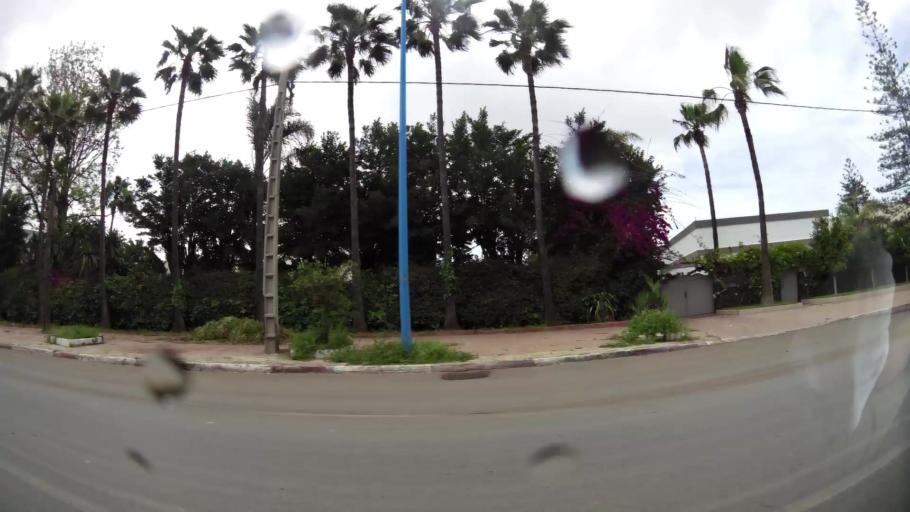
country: MA
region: Grand Casablanca
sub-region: Casablanca
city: Casablanca
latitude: 33.5493
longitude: -7.6253
